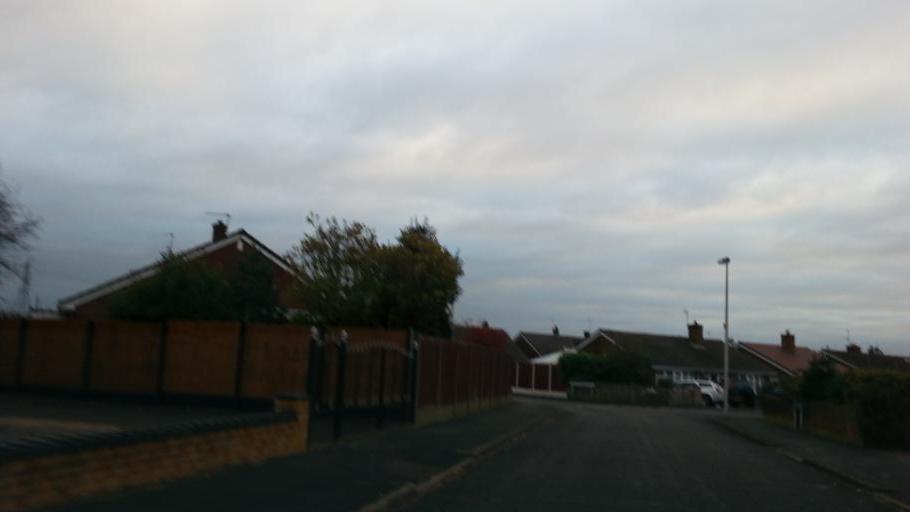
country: GB
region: England
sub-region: Sandwell
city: Wednesbury
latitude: 52.5475
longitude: -2.0412
